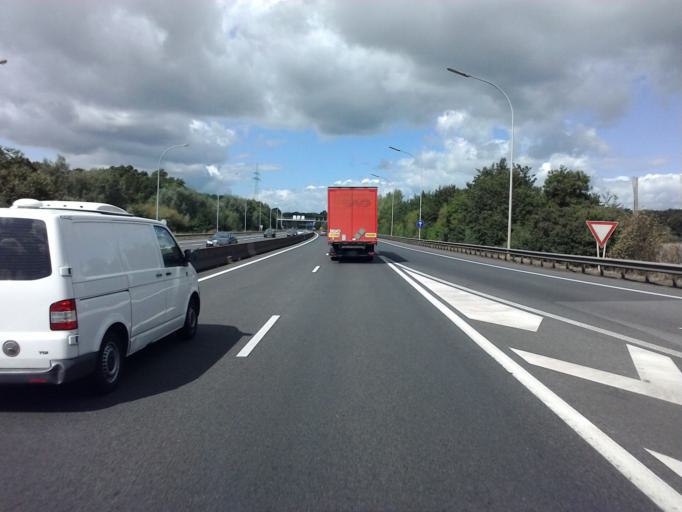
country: LU
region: Luxembourg
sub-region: Canton de Capellen
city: Garnich
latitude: 49.6361
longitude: 5.9675
